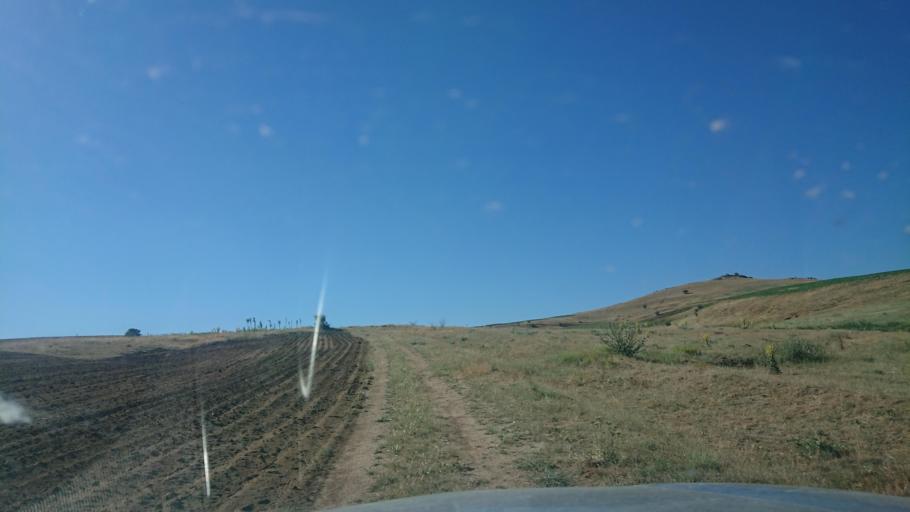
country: TR
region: Aksaray
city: Agacoren
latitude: 38.8408
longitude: 33.9323
